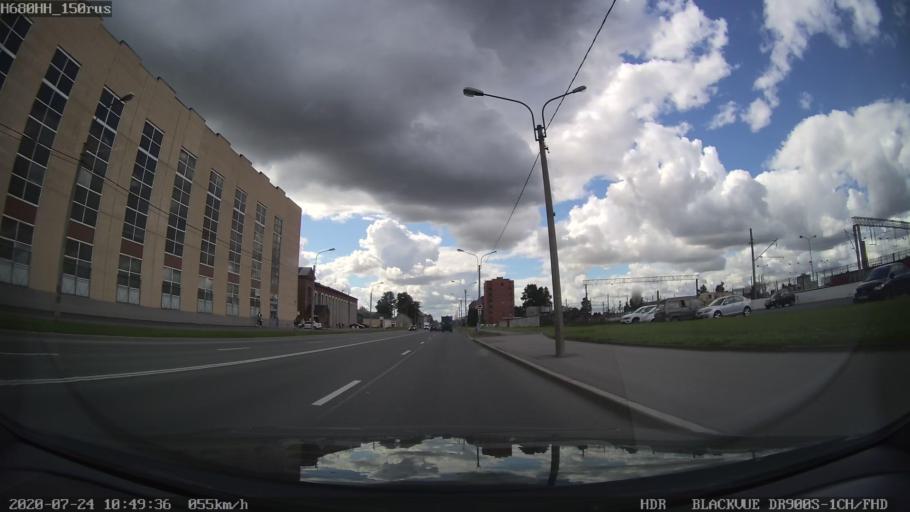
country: RU
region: St.-Petersburg
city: Admiralteisky
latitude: 59.9049
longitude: 30.3001
